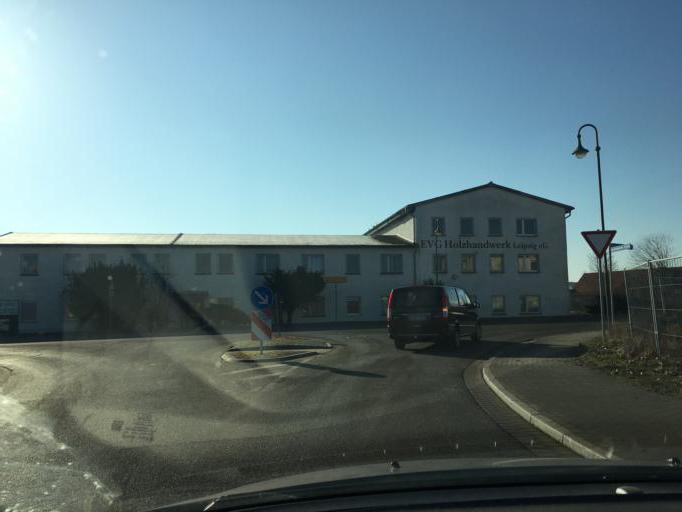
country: DE
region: Saxony
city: Grossposna
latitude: 51.2820
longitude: 12.4725
